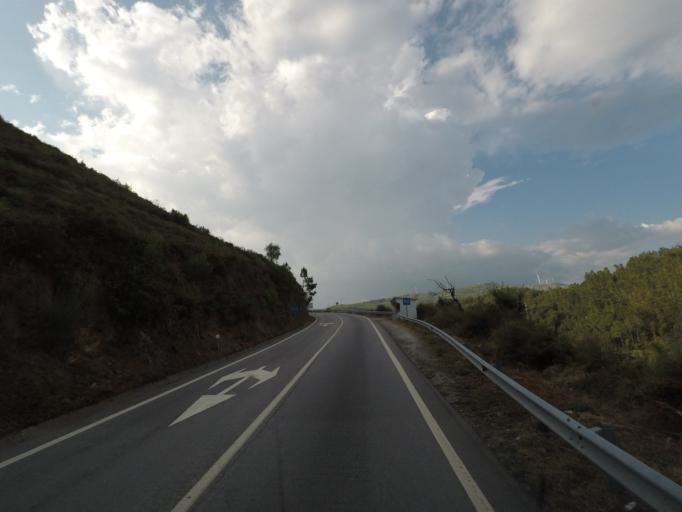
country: PT
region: Porto
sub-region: Baiao
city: Valadares
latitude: 41.1831
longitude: -7.9376
